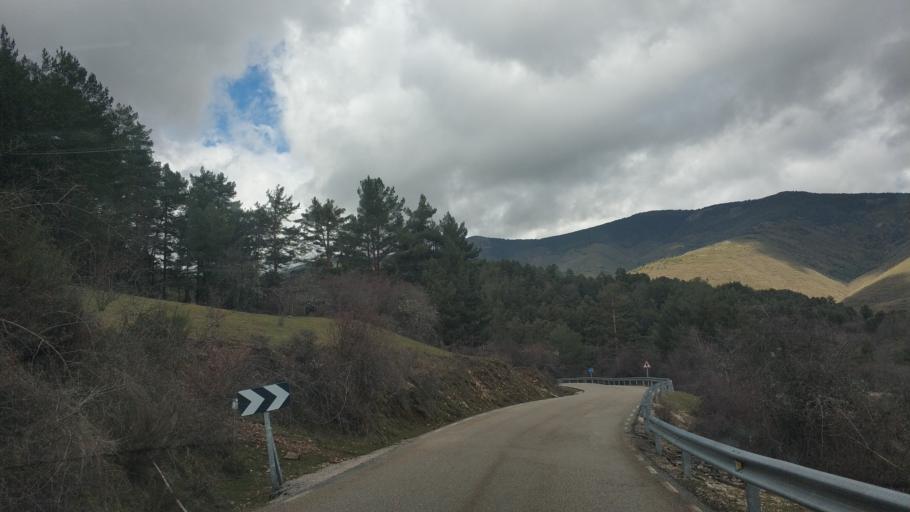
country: ES
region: Castille and Leon
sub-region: Provincia de Burgos
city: Neila
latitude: 42.0553
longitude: -3.0111
